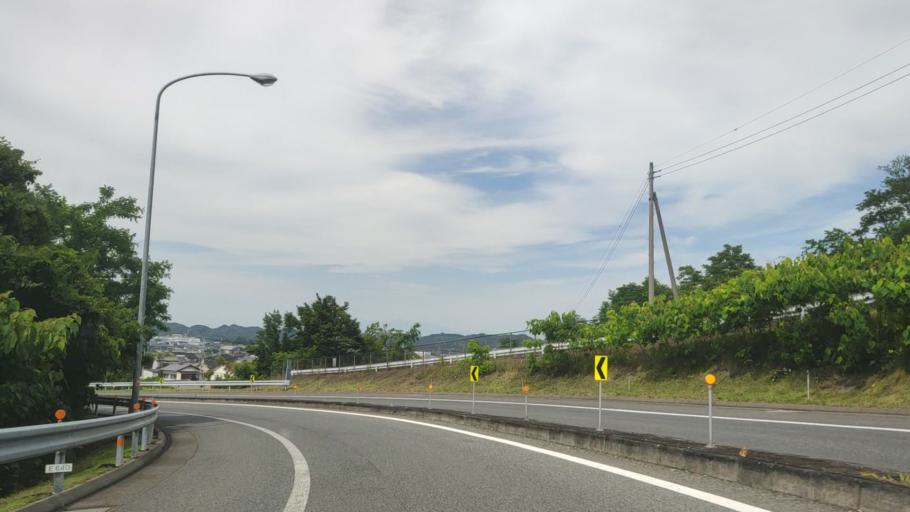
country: JP
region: Gunma
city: Tomioka
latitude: 36.2437
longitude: 138.8942
